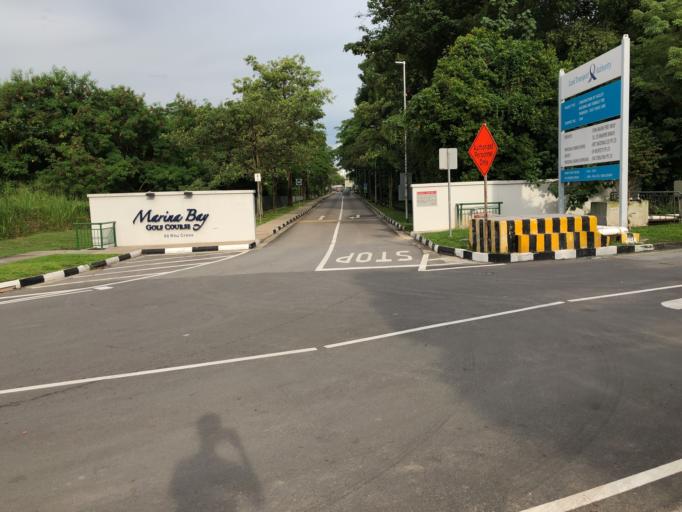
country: SG
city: Singapore
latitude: 1.2934
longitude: 103.8684
